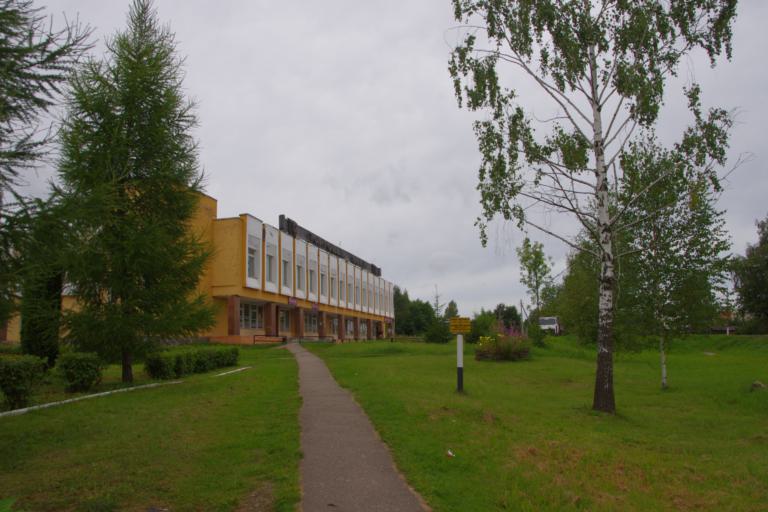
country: BY
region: Vitebsk
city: Chashniki
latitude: 55.3495
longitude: 29.3031
